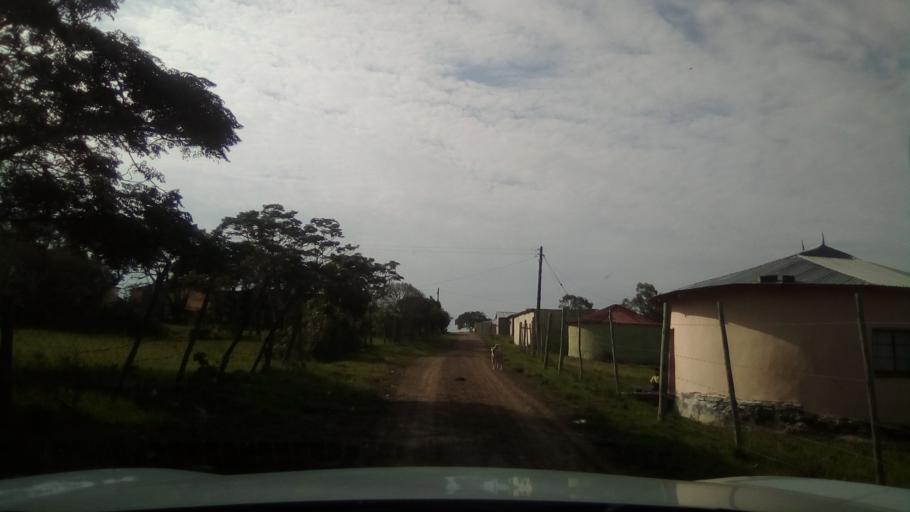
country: ZA
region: Eastern Cape
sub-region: Buffalo City Metropolitan Municipality
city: Bhisho
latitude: -33.0076
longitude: 27.3008
